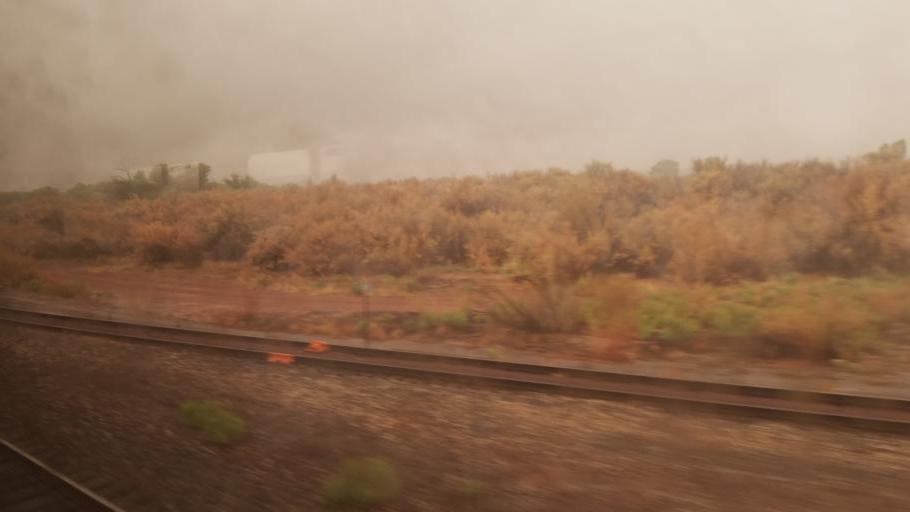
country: US
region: Arizona
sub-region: Navajo County
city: Holbrook
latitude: 34.9037
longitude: -110.2394
